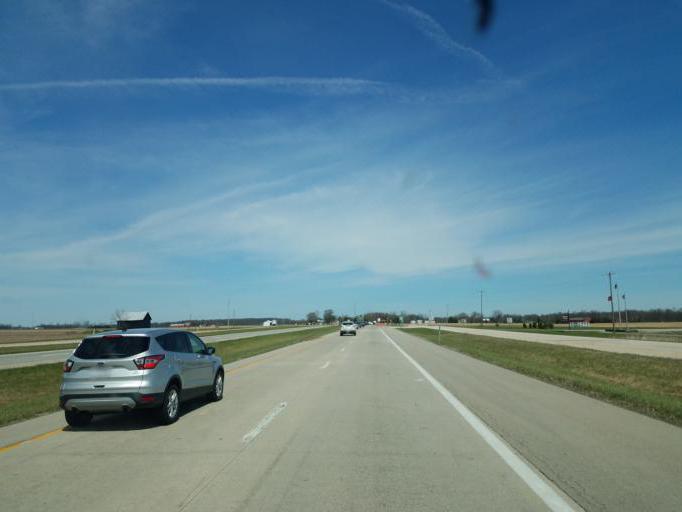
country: US
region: Ohio
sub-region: Marion County
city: Prospect
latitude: 40.4211
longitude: -83.0742
